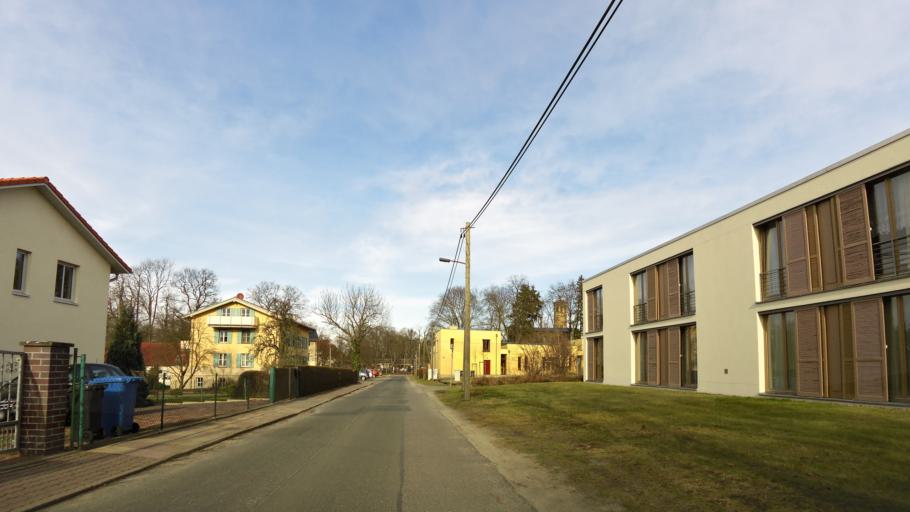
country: DE
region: Brandenburg
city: Michendorf
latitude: 52.3471
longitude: 13.0008
